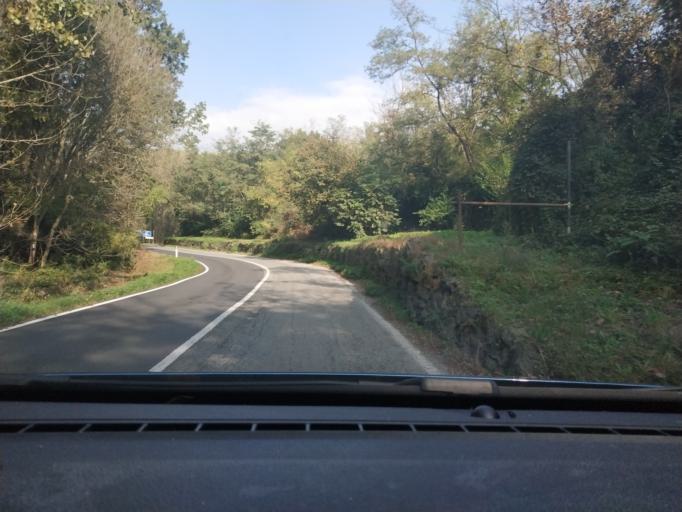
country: IT
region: Piedmont
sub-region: Provincia di Torino
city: Cascinette d'Ivrea
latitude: 45.4872
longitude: 7.9017
